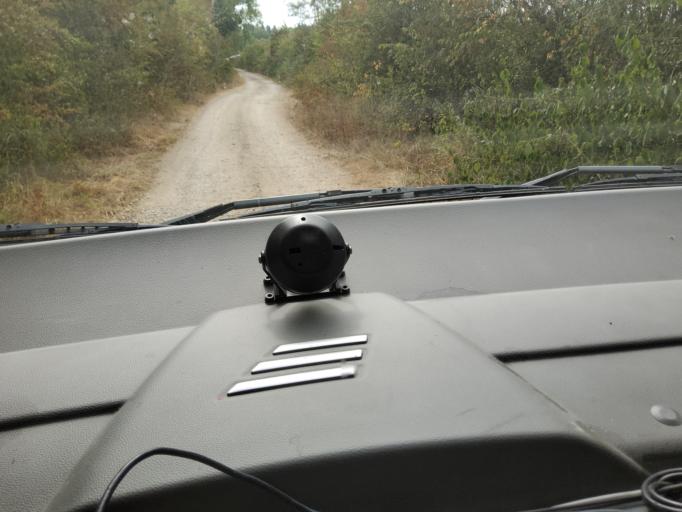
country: FR
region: Franche-Comte
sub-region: Departement du Jura
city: Choisey
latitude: 47.0149
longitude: 5.4801
